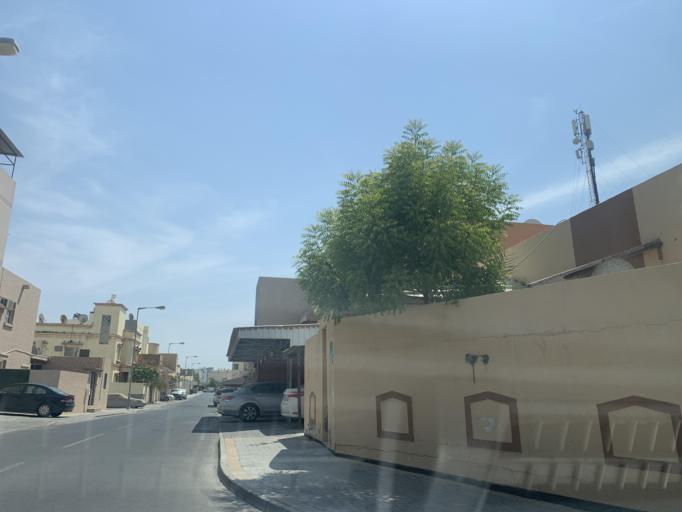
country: BH
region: Central Governorate
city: Madinat Hamad
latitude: 26.1365
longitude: 50.5007
